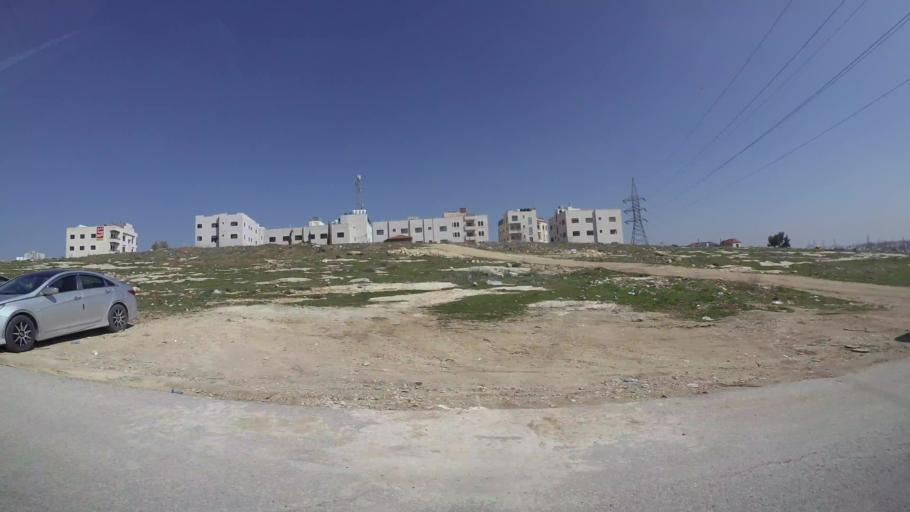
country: JO
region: Amman
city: Al Bunayyat ash Shamaliyah
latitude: 31.8923
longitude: 35.8994
